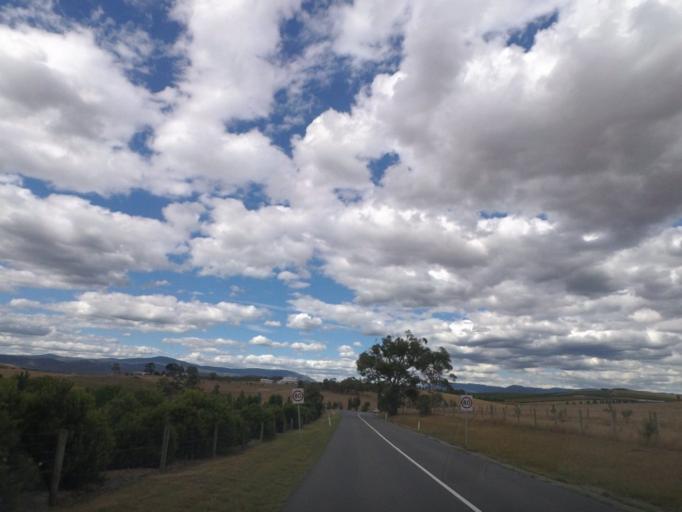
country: AU
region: Victoria
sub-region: Yarra Ranges
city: Yarra Glen
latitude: -37.6447
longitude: 145.4012
